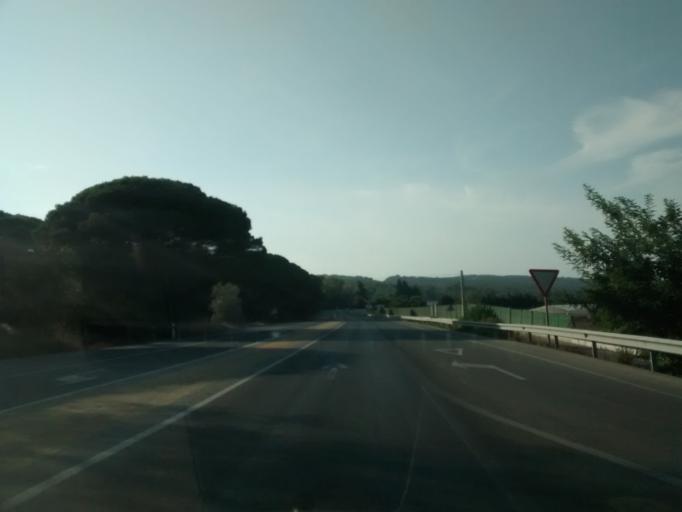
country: ES
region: Andalusia
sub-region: Provincia de Cadiz
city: Barbate de Franco
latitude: 36.2163
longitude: -5.9434
